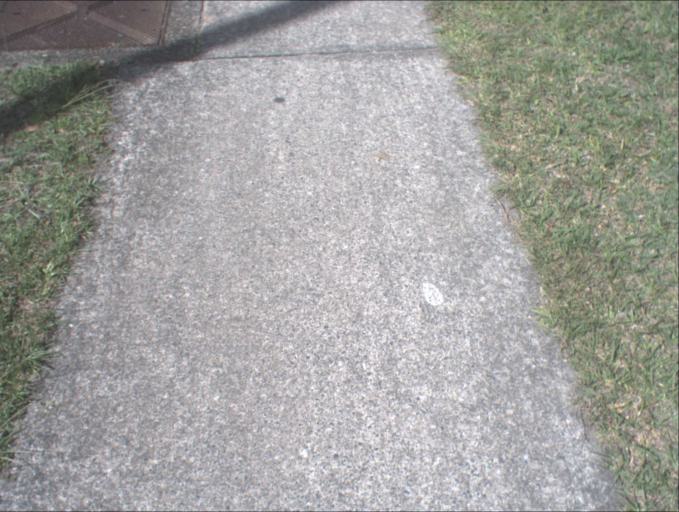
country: AU
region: Queensland
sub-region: Logan
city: Waterford West
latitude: -27.6807
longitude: 153.1082
